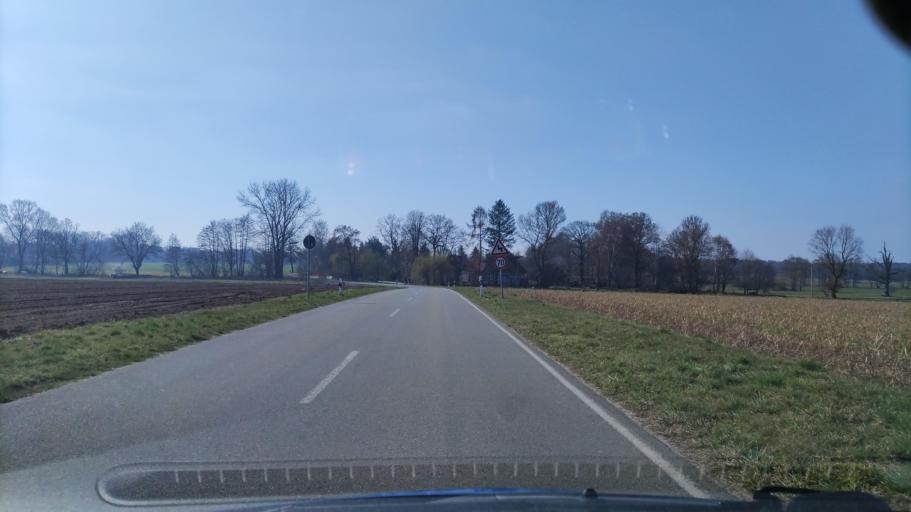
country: DE
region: Lower Saxony
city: Kusten
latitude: 53.0006
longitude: 11.0653
